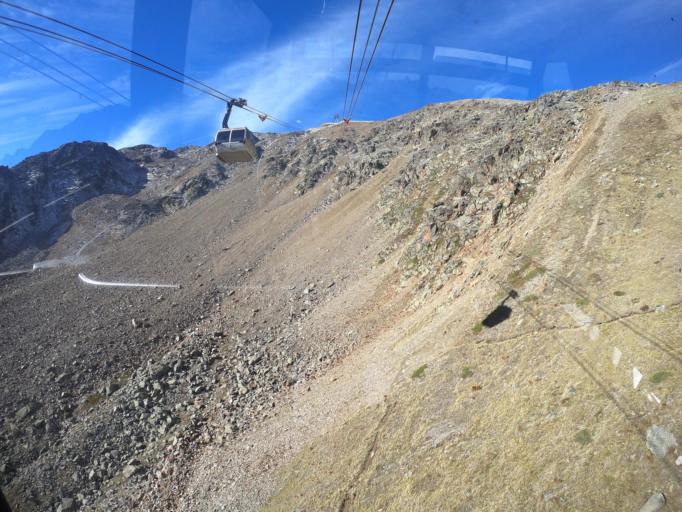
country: AT
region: Tyrol
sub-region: Politischer Bezirk Imst
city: Soelden
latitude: 46.9468
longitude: 10.9773
